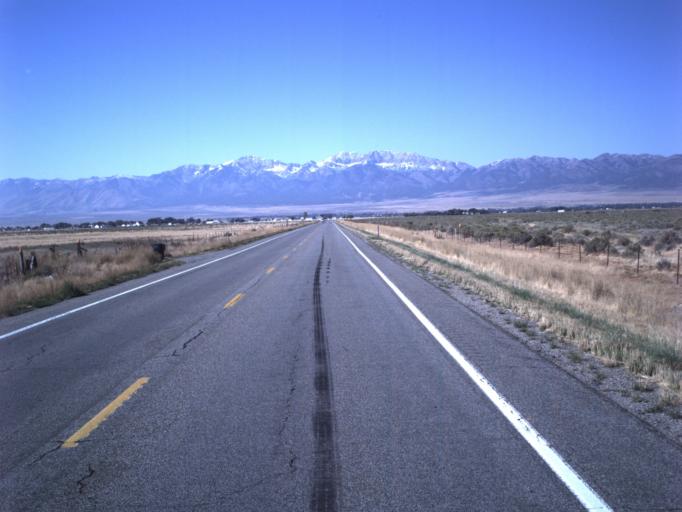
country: US
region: Utah
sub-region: Tooele County
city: Erda
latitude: 40.6115
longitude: -112.3768
